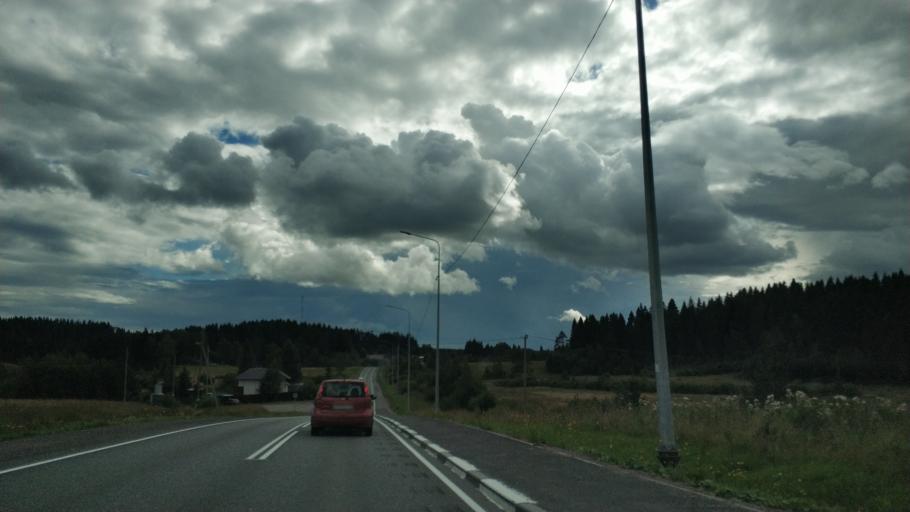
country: RU
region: Republic of Karelia
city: Khelyulya
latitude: 61.7636
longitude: 30.6560
